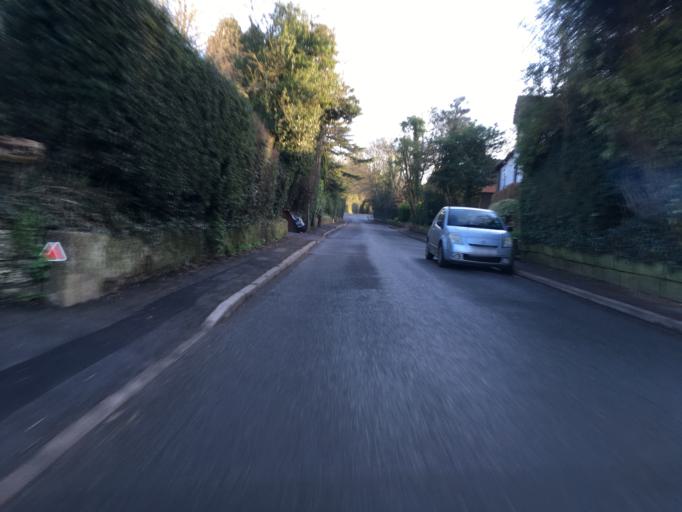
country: GB
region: England
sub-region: Warwickshire
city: Stratford-upon-Avon
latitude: 52.2359
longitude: -1.6880
